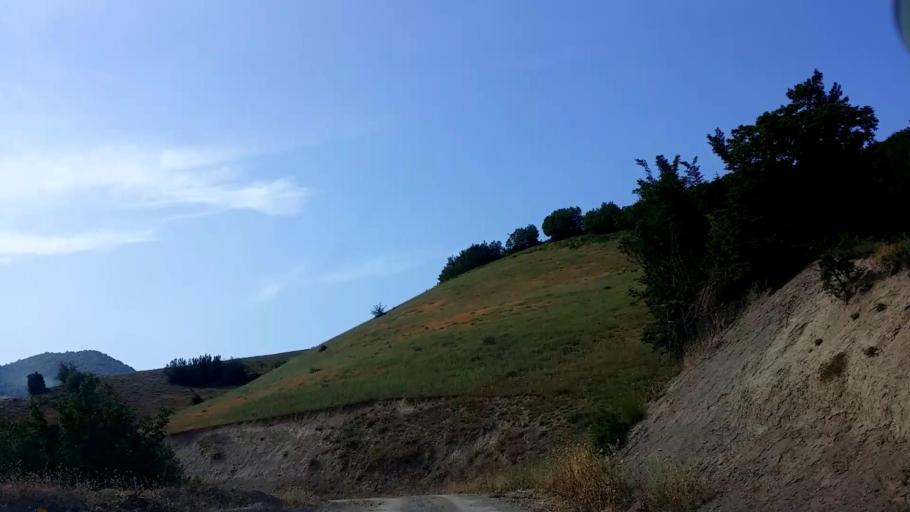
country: IR
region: Mazandaran
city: Chalus
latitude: 36.5476
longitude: 51.2966
